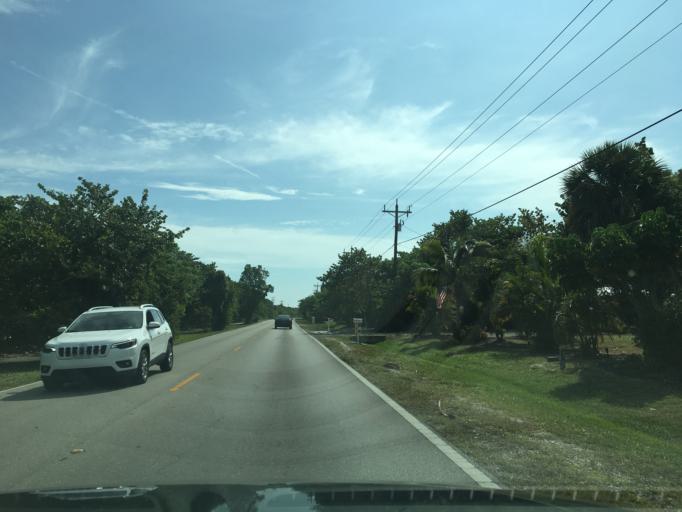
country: US
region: Florida
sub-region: Lee County
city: Saint James City
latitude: 26.4654
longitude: -82.1517
